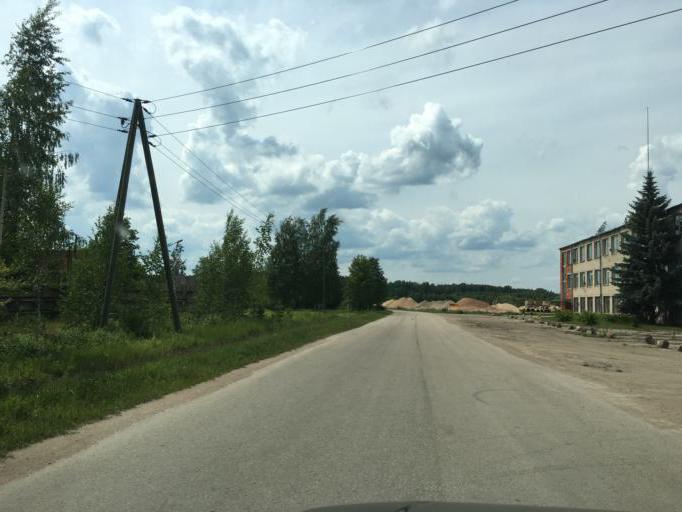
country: LV
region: Balvu Rajons
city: Balvi
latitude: 57.1441
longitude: 27.2515
